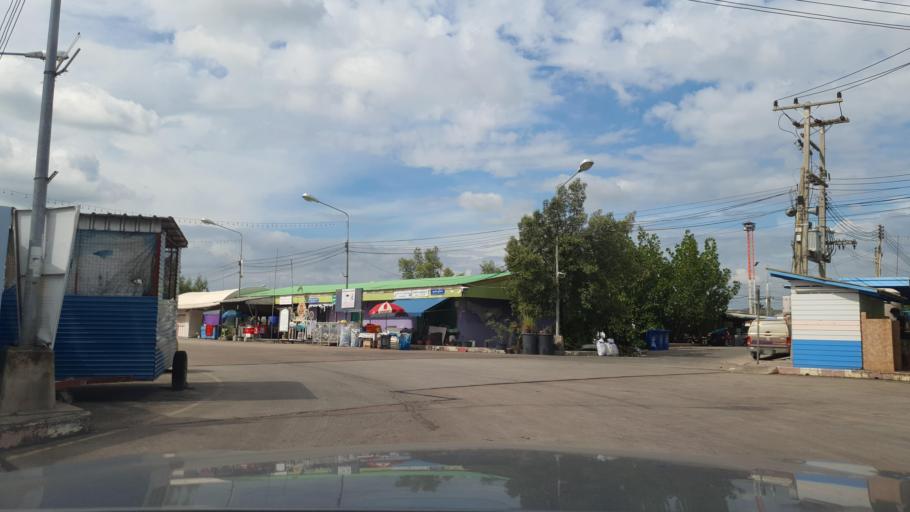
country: TH
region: Chon Buri
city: Chon Buri
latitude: 13.3700
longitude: 100.9785
